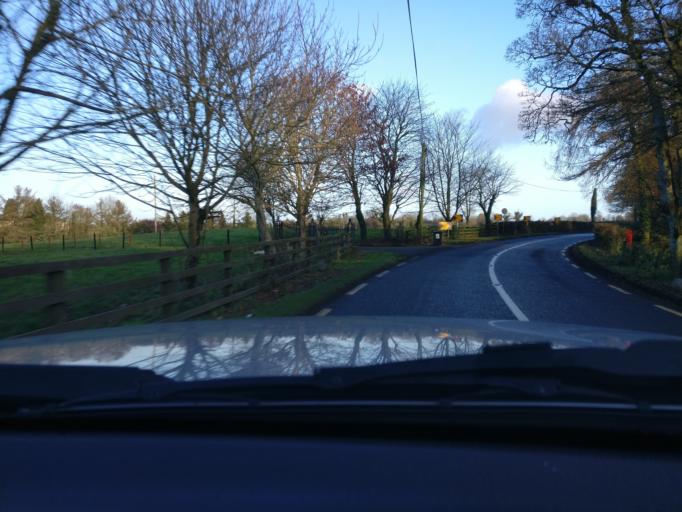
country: IE
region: Ulster
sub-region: An Cabhan
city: Kingscourt
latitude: 53.7976
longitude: -6.7138
